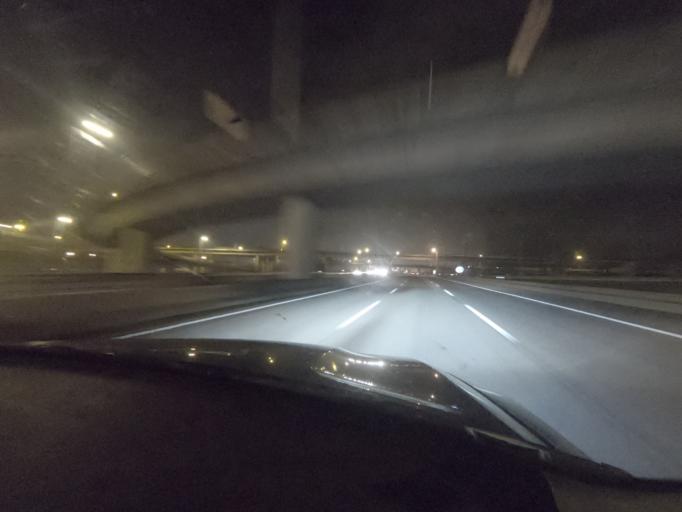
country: PT
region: Lisbon
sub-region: Alenquer
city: Carregado
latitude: 39.0187
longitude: -8.9658
